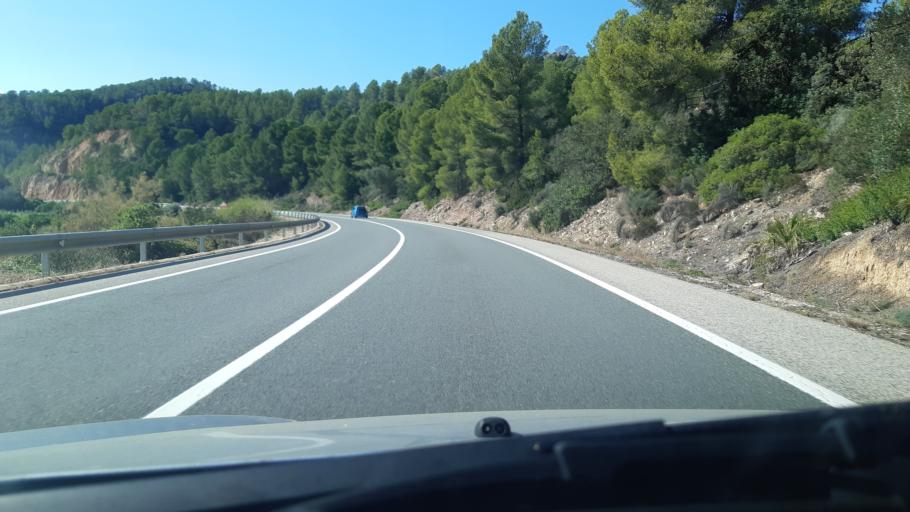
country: ES
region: Catalonia
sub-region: Provincia de Tarragona
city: Benifallet
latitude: 40.9589
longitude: 0.4912
